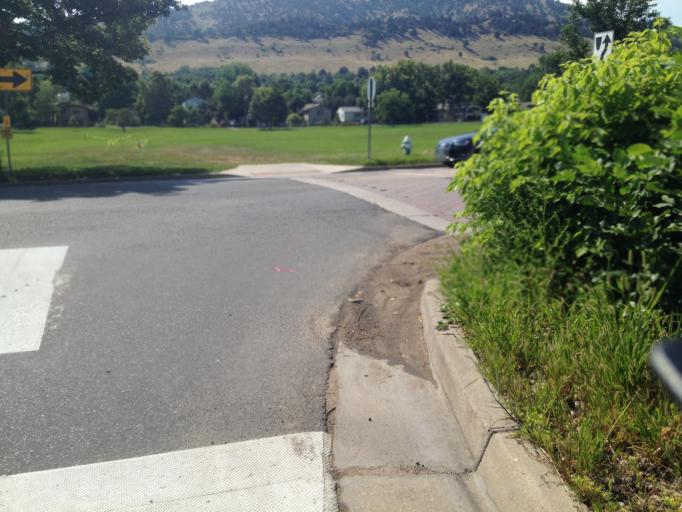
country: US
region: Colorado
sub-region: Boulder County
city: Boulder
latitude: 40.0267
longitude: -105.2854
